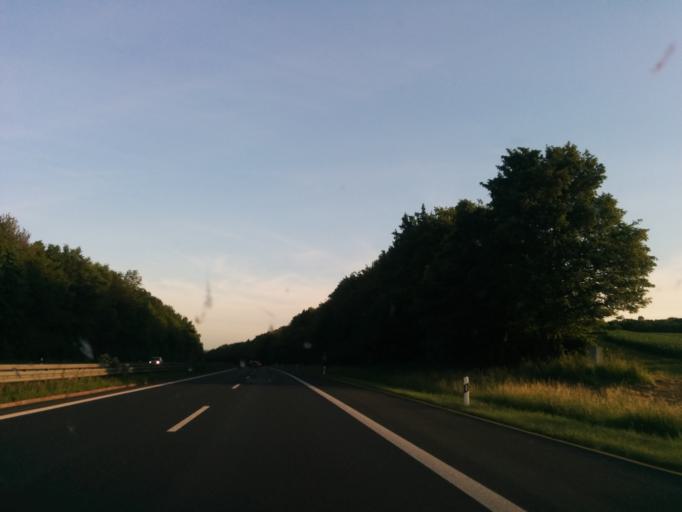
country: DE
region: Bavaria
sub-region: Regierungsbezirk Unterfranken
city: Rimpar
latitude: 49.8773
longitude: 9.9932
